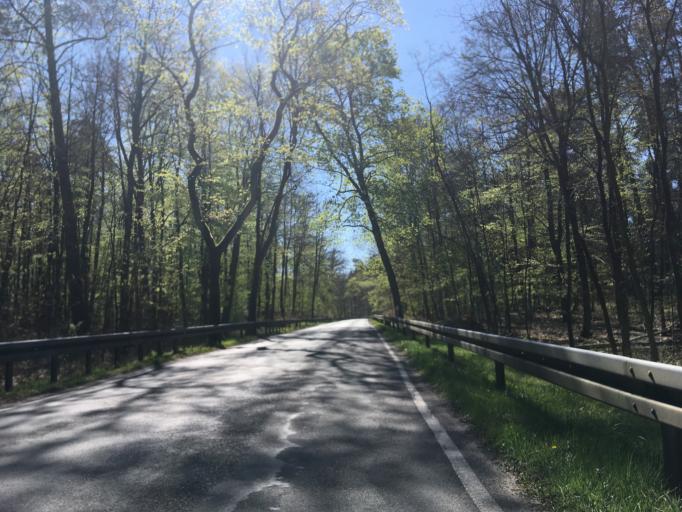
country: DE
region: Brandenburg
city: Bernau bei Berlin
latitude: 52.7184
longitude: 13.5725
